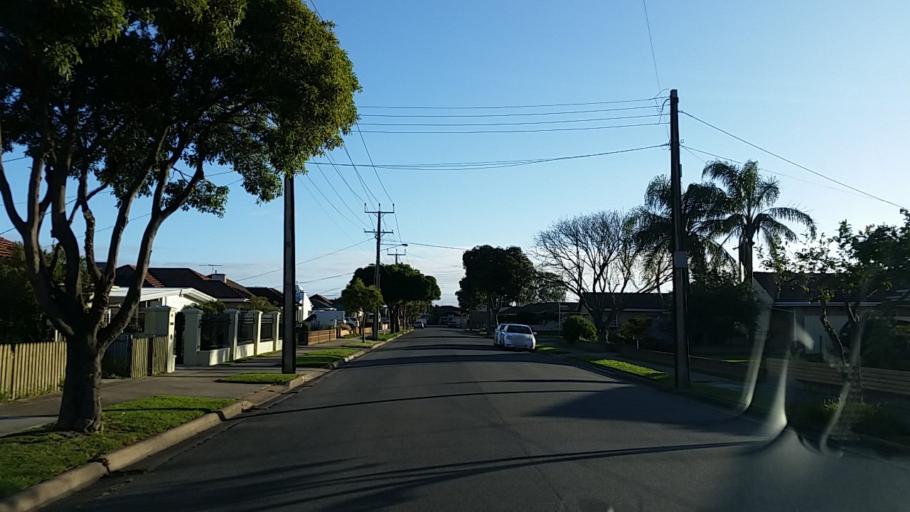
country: AU
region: South Australia
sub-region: Charles Sturt
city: Findon
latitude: -34.8958
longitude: 138.5370
